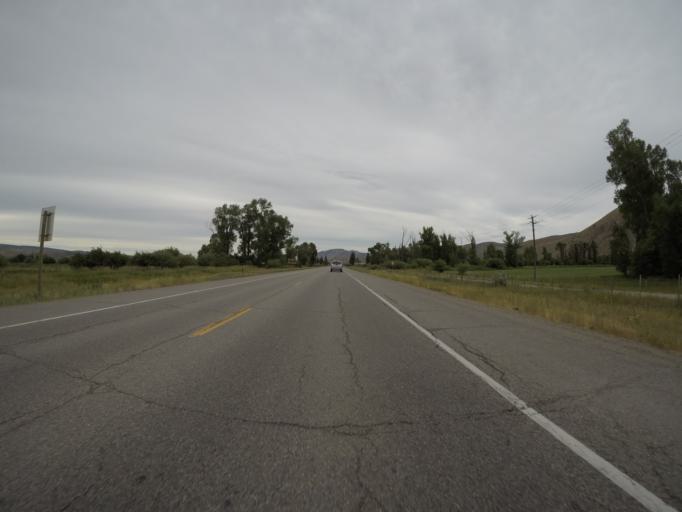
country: US
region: Idaho
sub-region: Bear Lake County
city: Montpelier
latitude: 42.0917
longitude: -110.9502
